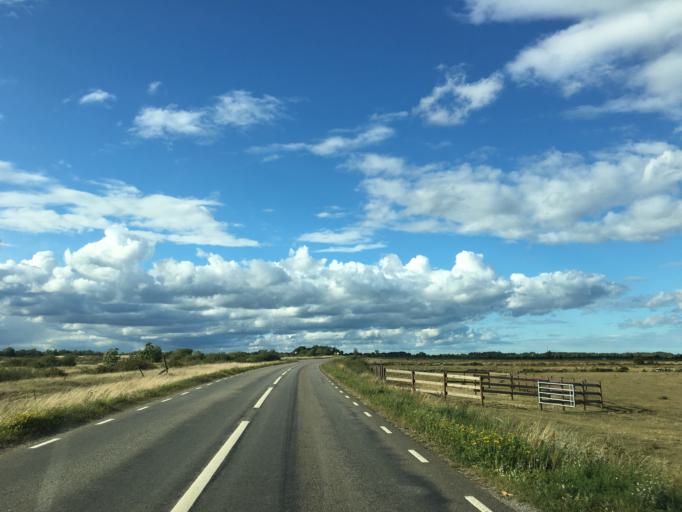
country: SE
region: Kalmar
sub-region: Morbylanga Kommun
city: Moerbylanga
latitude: 56.4884
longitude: 16.4265
